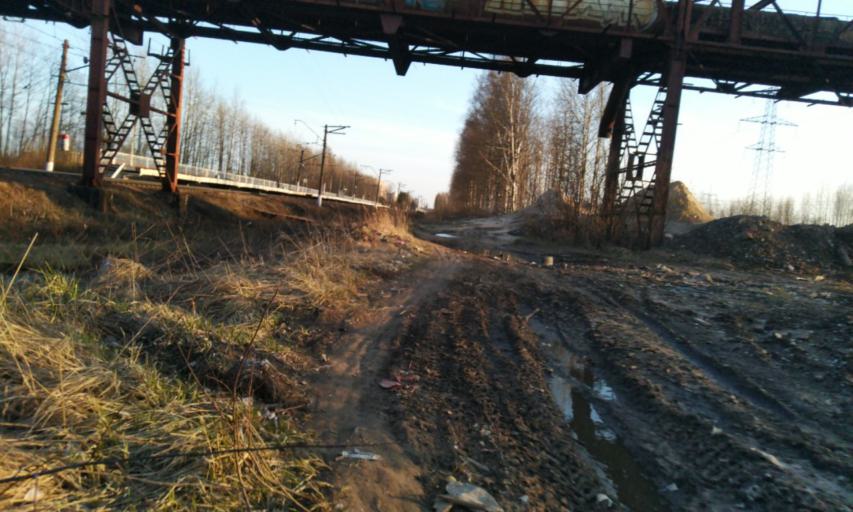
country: RU
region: Leningrad
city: Novoye Devyatkino
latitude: 60.0787
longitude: 30.4612
